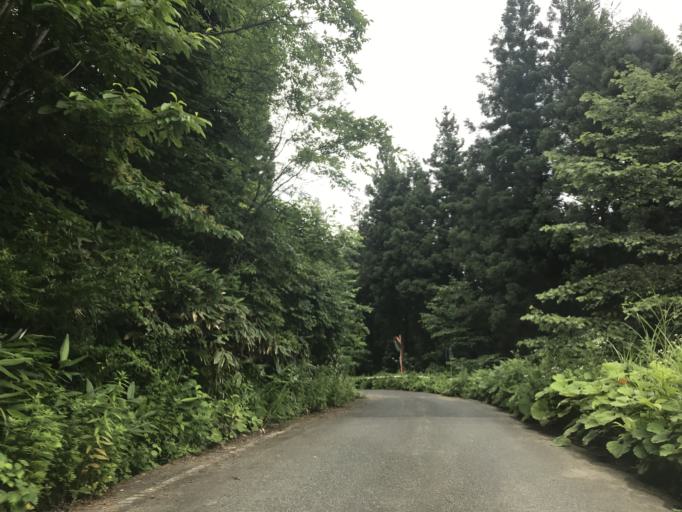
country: JP
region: Iwate
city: Ichinoseki
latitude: 38.9557
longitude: 140.8866
